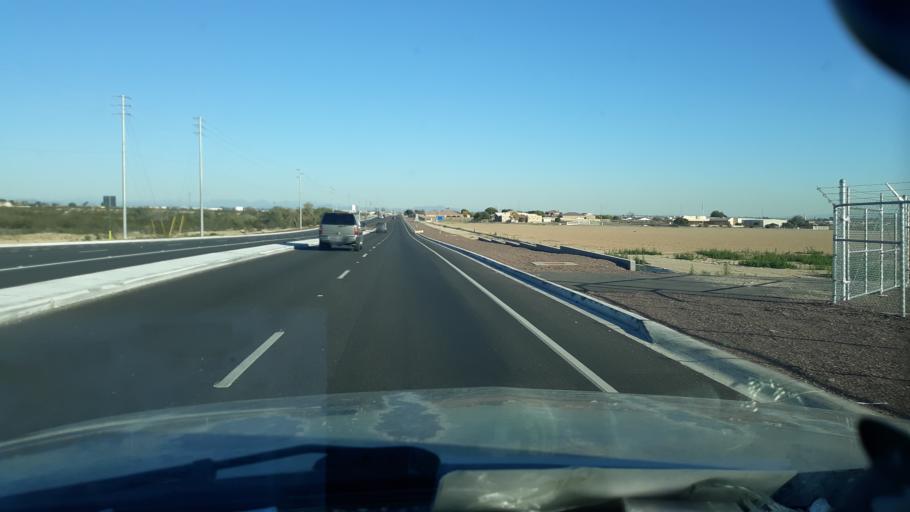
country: US
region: Arizona
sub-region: Maricopa County
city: Citrus Park
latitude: 33.5662
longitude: -112.4441
